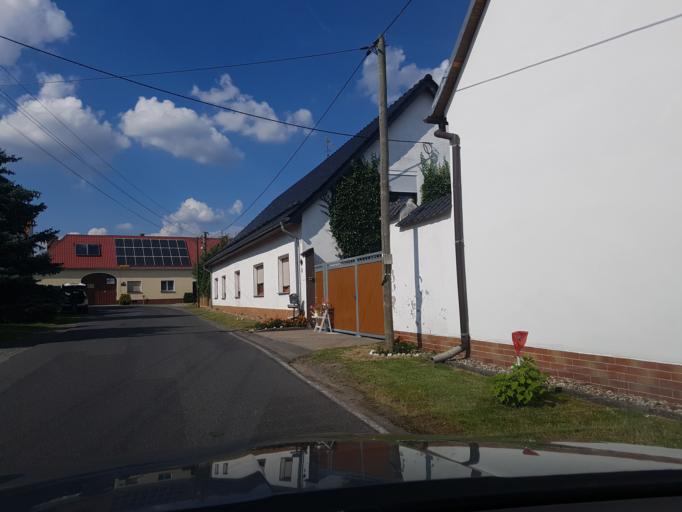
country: DE
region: Brandenburg
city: Schonborn
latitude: 51.6708
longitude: 13.4733
